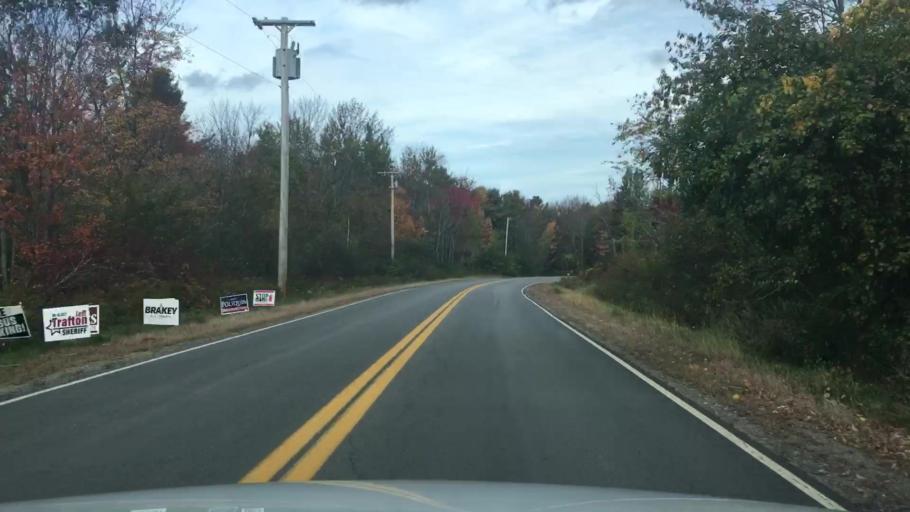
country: US
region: Maine
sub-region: Waldo County
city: Searsmont
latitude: 44.3992
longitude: -69.1354
